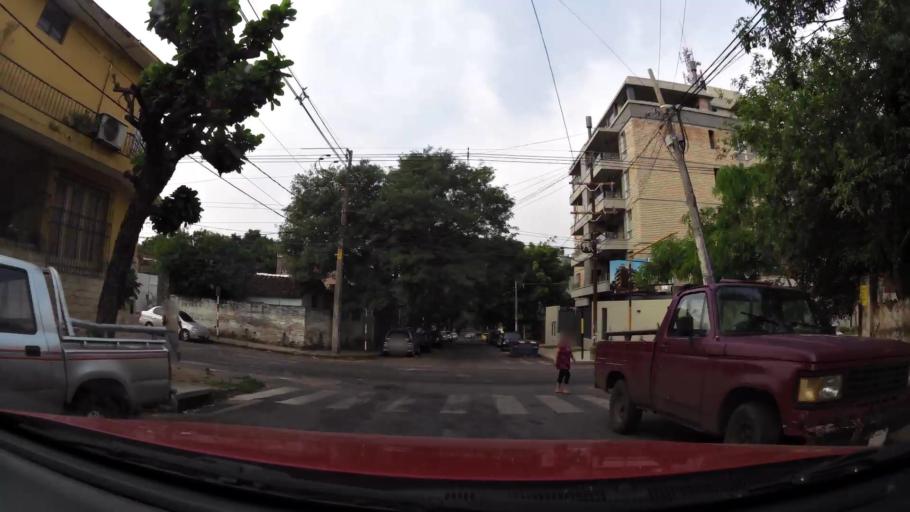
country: PY
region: Asuncion
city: Asuncion
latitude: -25.2975
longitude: -57.6097
